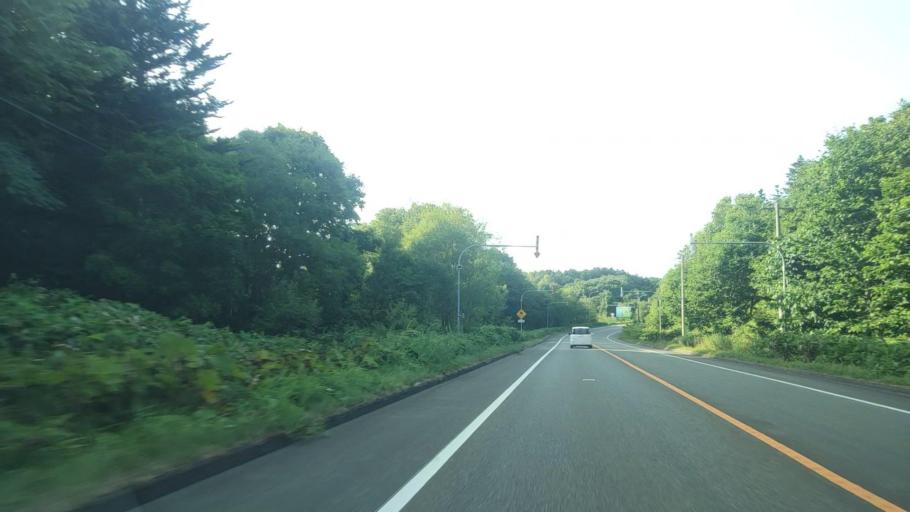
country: JP
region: Hokkaido
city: Makubetsu
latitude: 45.0771
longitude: 141.7537
